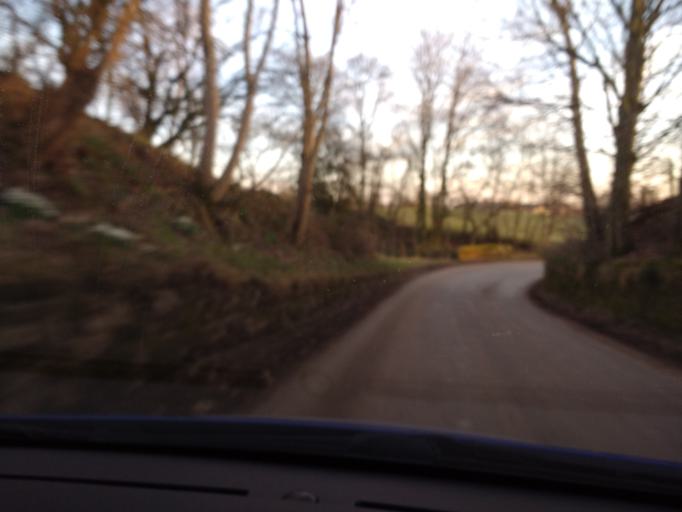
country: GB
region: England
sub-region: Cumbria
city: Appleby-in-Westmorland
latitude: 54.6158
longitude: -2.4740
